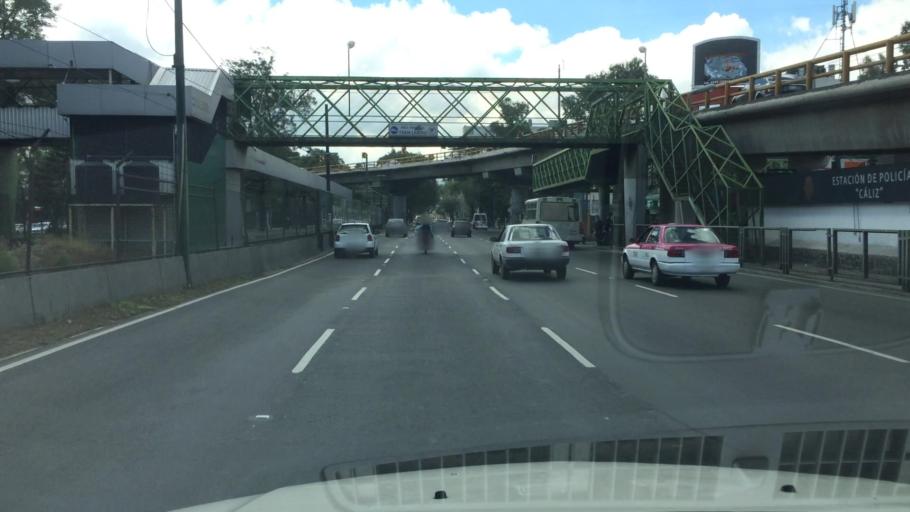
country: MX
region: Mexico City
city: Tlalpan
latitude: 19.3185
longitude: -99.1387
